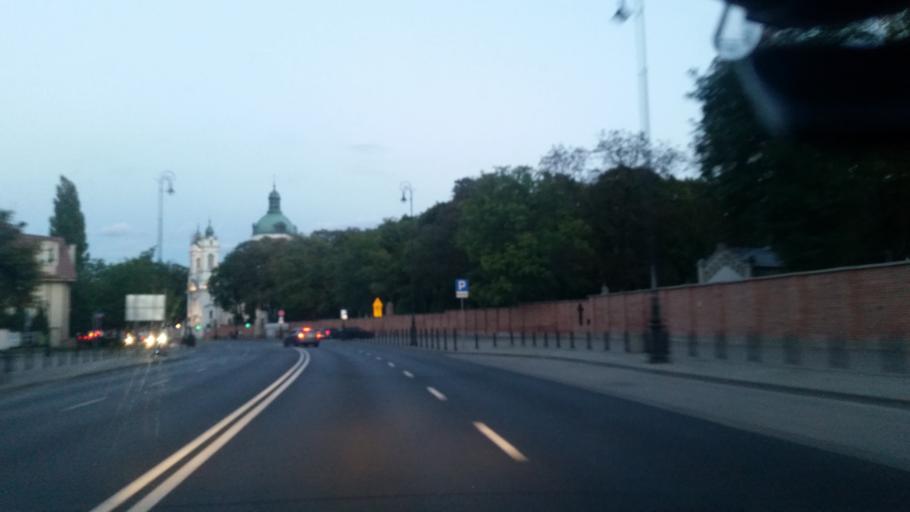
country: PL
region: Masovian Voivodeship
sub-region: Warszawa
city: Zoliborz
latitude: 52.2539
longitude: 20.9750
